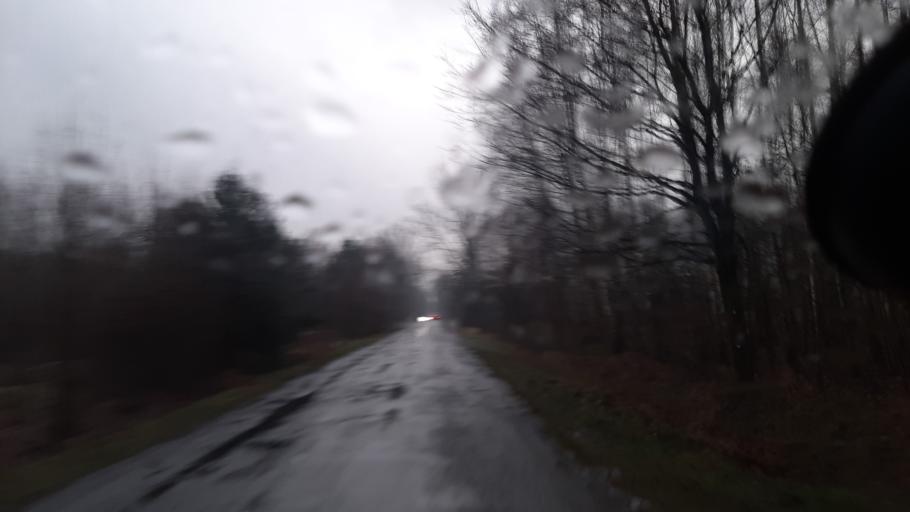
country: PL
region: Lublin Voivodeship
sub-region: Powiat lubartowski
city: Firlej
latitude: 51.5219
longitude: 22.4985
